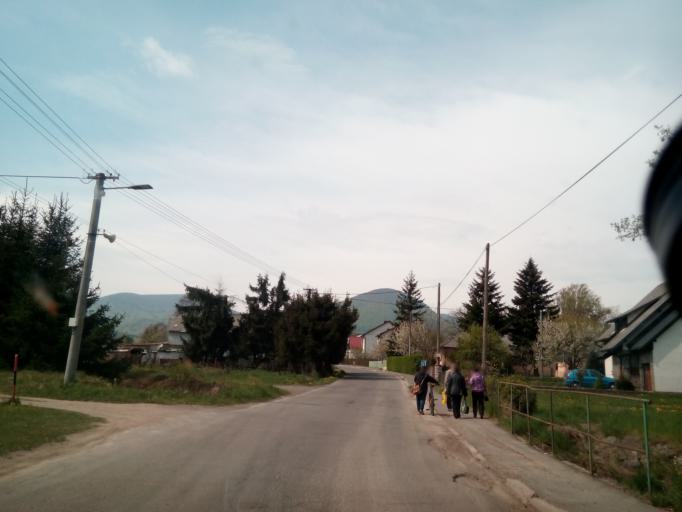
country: SK
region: Presovsky
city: Giraltovce
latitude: 48.9980
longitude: 21.5320
